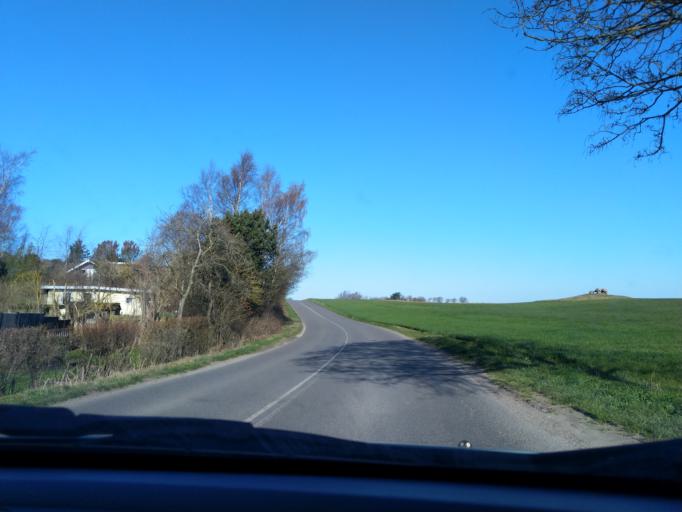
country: DK
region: Zealand
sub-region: Kalundborg Kommune
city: Kalundborg
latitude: 55.7268
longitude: 11.0006
